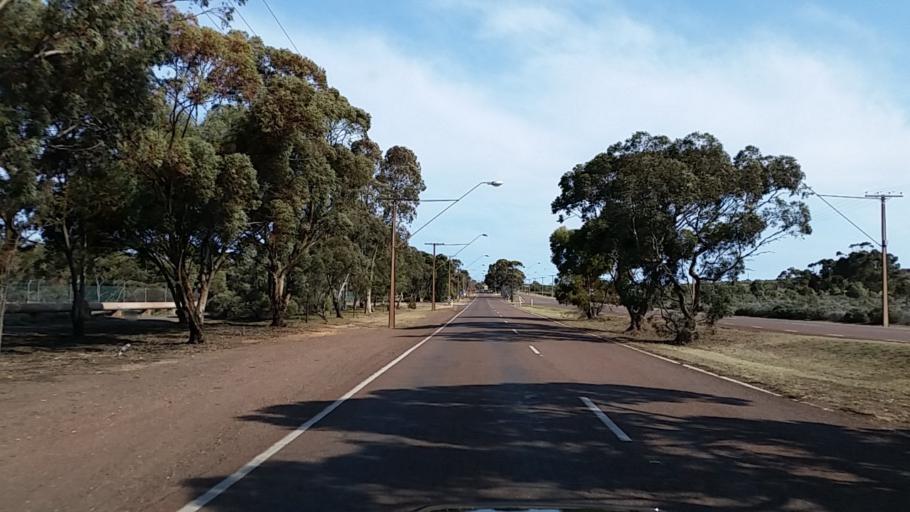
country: AU
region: South Australia
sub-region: Whyalla
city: Whyalla
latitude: -33.0135
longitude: 137.5753
